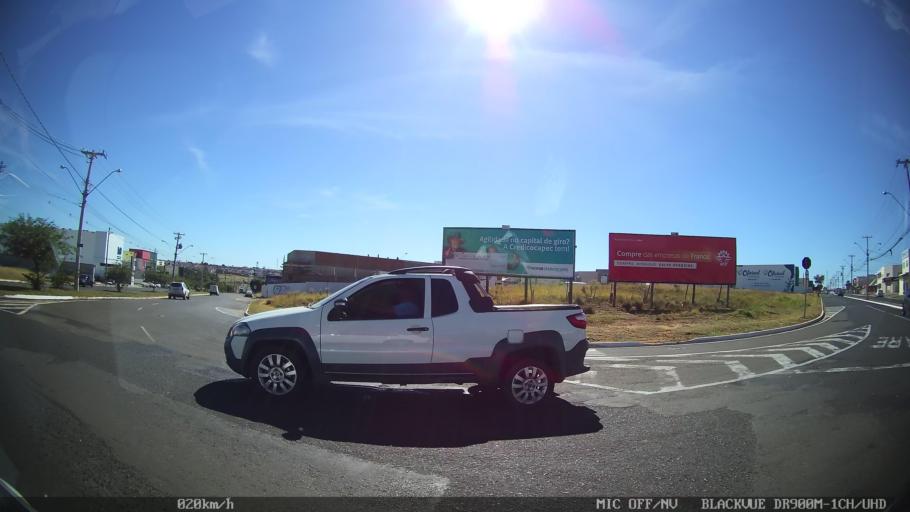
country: BR
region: Sao Paulo
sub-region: Franca
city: Franca
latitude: -20.5419
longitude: -47.3751
